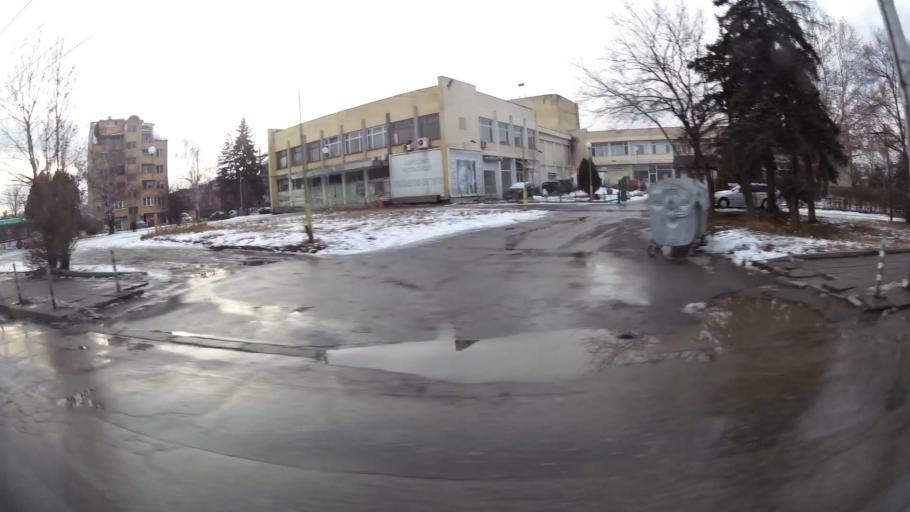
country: BG
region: Sofia-Capital
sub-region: Stolichna Obshtina
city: Sofia
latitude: 42.7229
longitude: 23.3429
